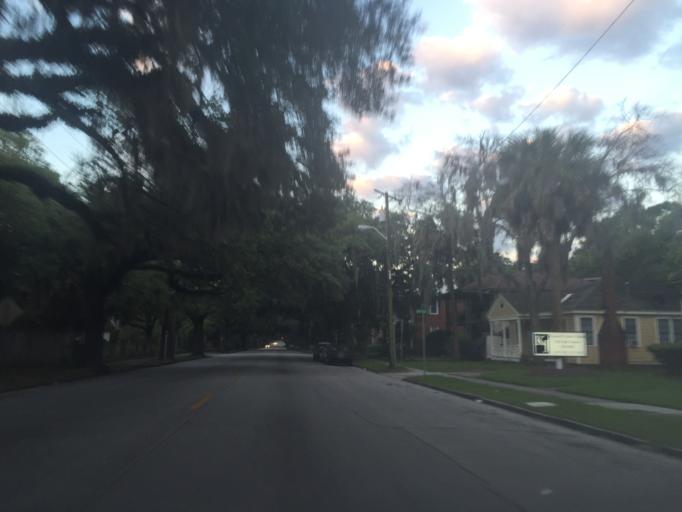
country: US
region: Georgia
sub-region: Chatham County
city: Savannah
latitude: 32.0489
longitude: -81.1035
